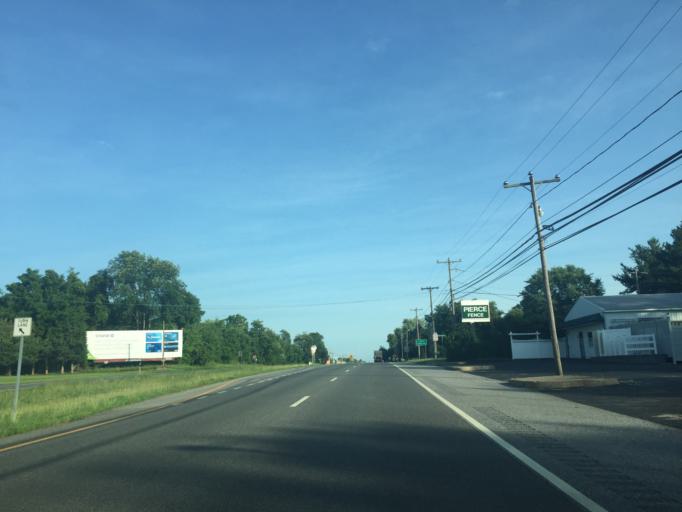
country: US
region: Delaware
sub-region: Kent County
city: Cheswold
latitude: 39.2287
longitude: -75.5790
